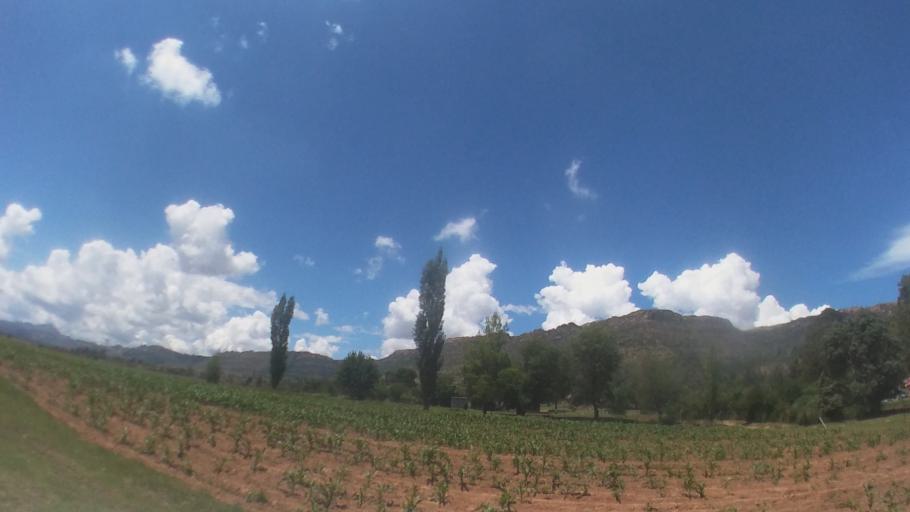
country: LS
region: Maseru
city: Nako
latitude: -29.6197
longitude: 27.5121
